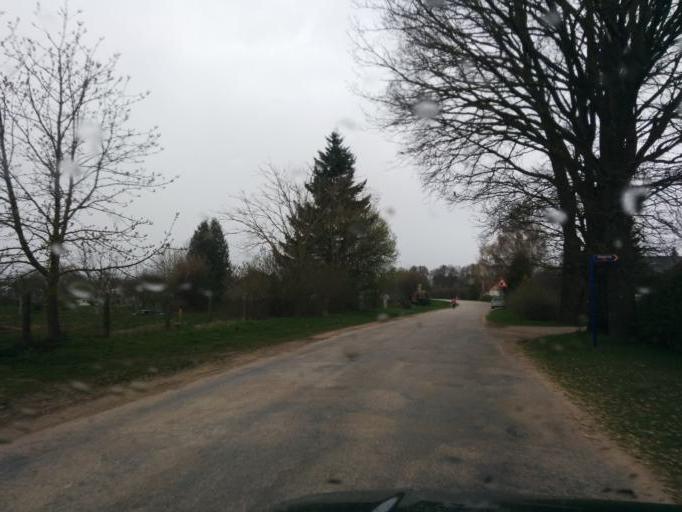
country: LV
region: Lecava
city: Iecava
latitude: 56.5972
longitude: 24.1877
